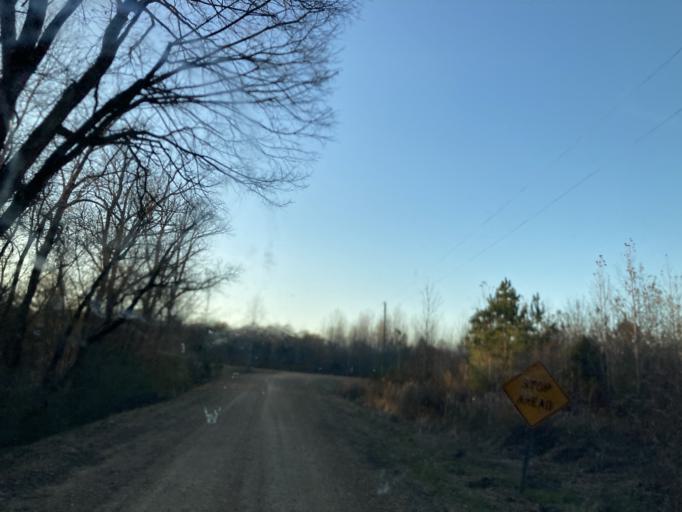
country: US
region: Mississippi
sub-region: Yazoo County
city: Yazoo City
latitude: 32.9720
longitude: -90.2639
